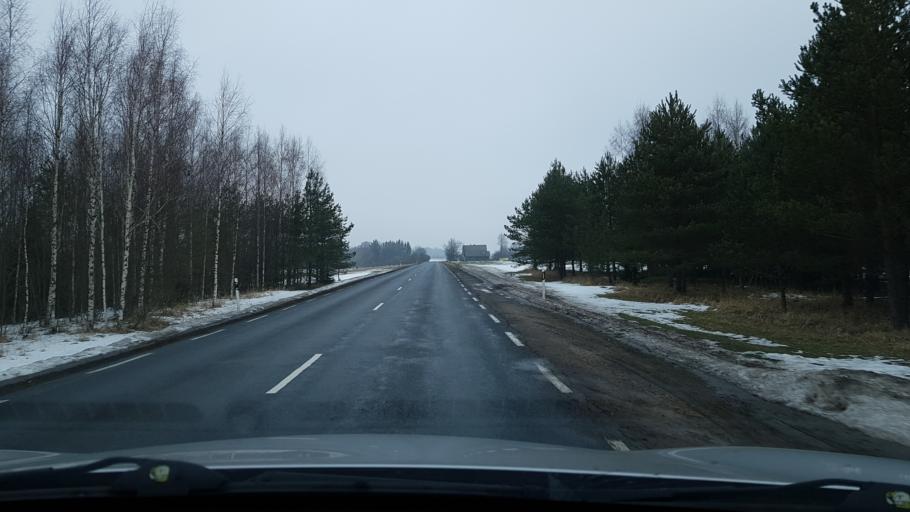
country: EE
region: Valgamaa
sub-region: Torva linn
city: Torva
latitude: 58.1237
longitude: 25.9925
